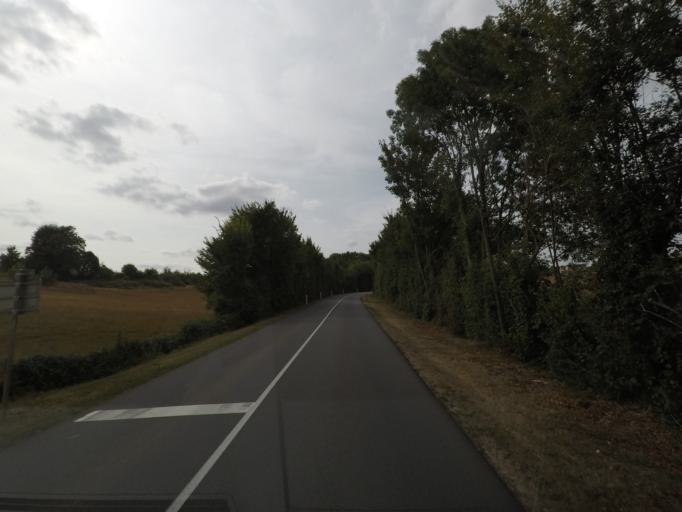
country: FR
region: Poitou-Charentes
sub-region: Departement de la Charente
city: Nanteuil-en-Vallee
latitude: 46.0027
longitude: 0.3176
